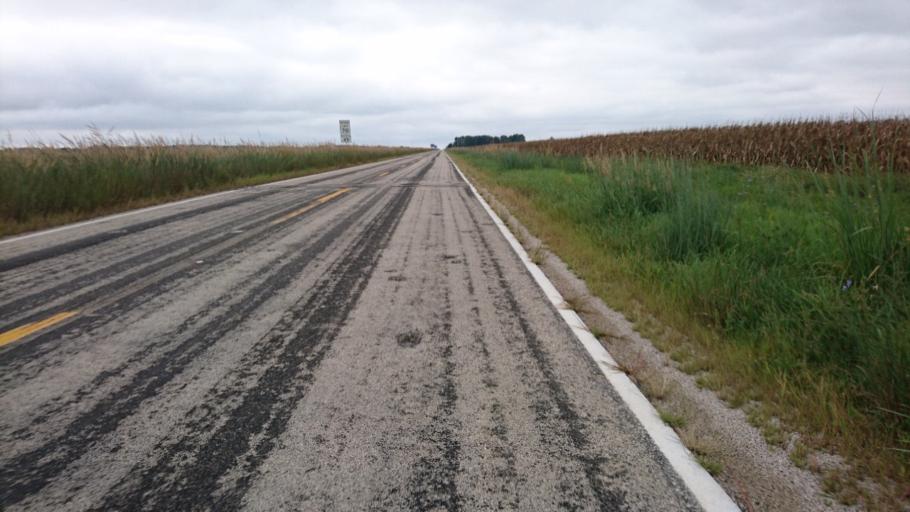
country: US
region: Illinois
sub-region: Montgomery County
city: Raymond
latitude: 39.3124
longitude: -89.6430
